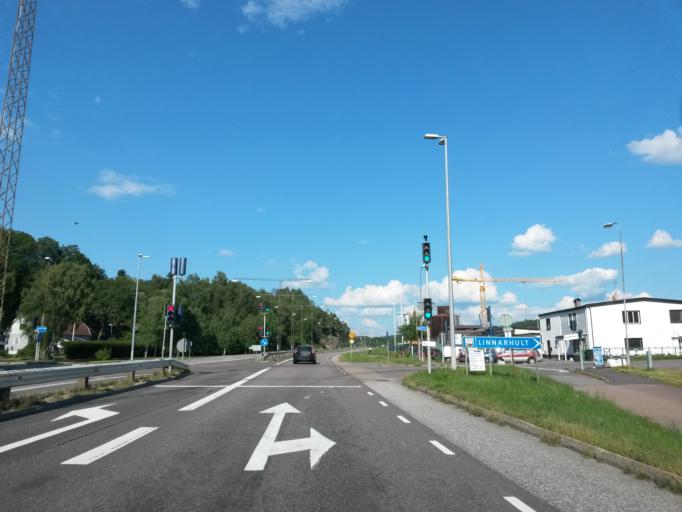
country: SE
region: Vaestra Goetaland
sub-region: Goteborg
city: Eriksbo
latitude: 57.7740
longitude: 12.0553
